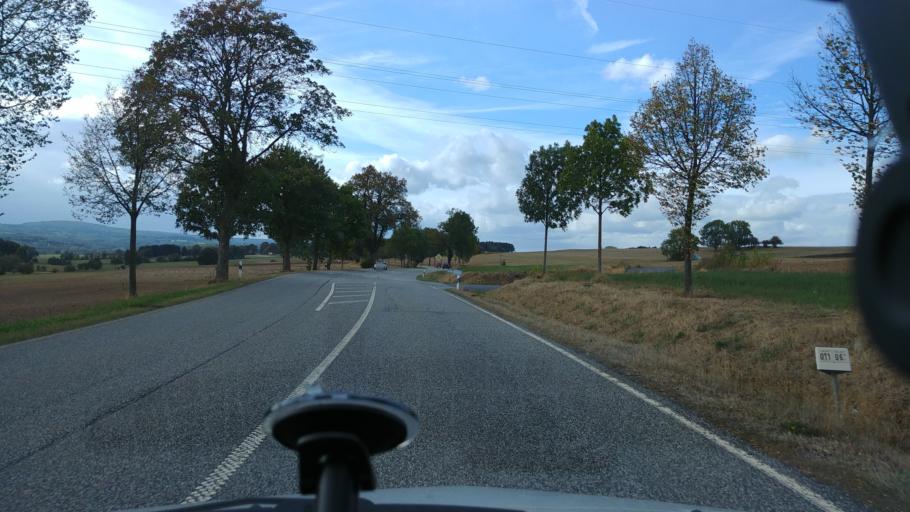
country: DE
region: Hesse
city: Herbstein
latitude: 50.5378
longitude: 9.3800
